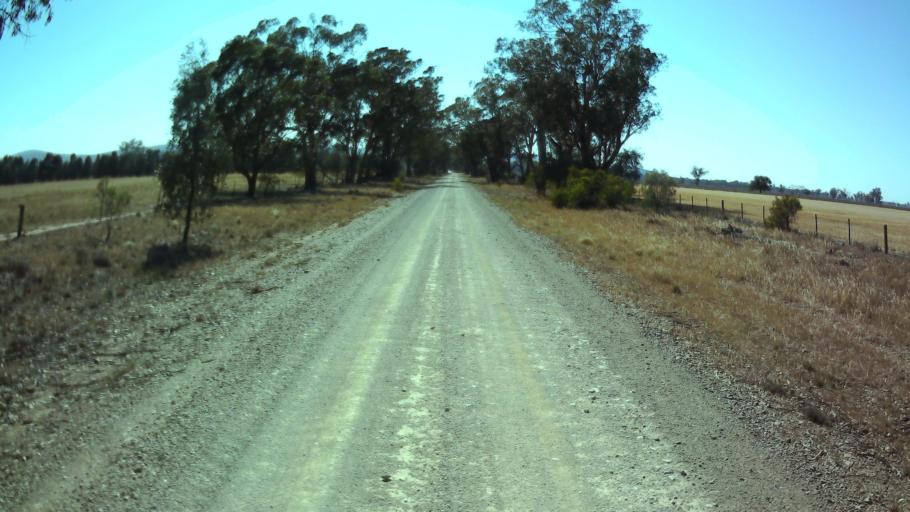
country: AU
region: New South Wales
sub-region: Weddin
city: Grenfell
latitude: -33.9434
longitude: 147.8563
